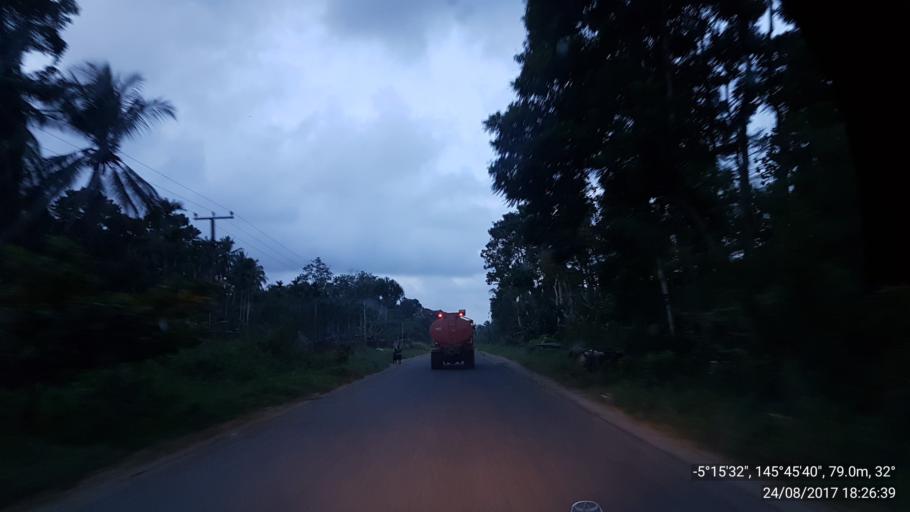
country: PG
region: Madang
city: Madang
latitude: -5.2592
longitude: 145.7611
